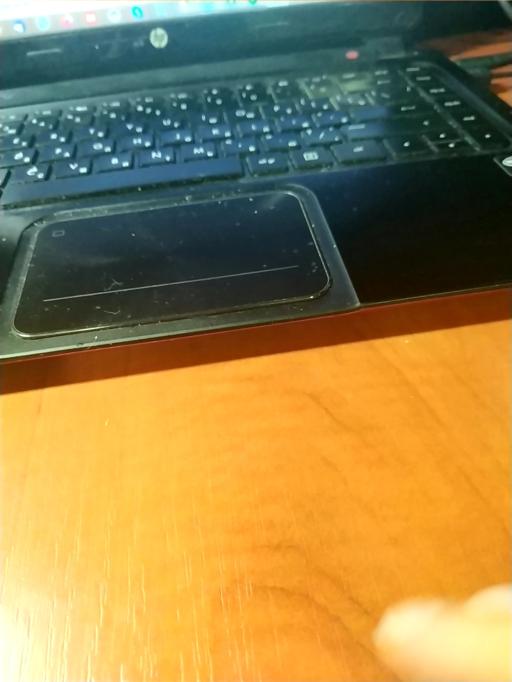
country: RU
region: Tverskaya
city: Vyshniy Volochek
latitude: 57.3947
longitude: 34.5275
